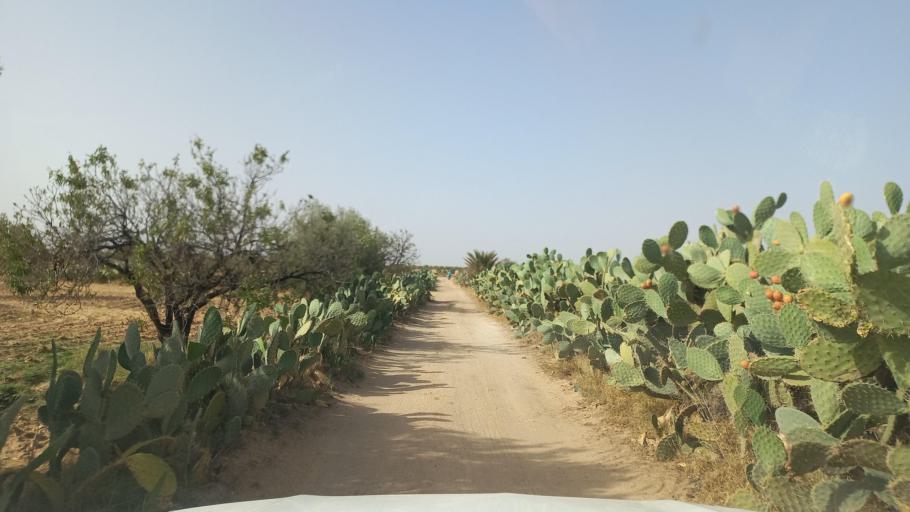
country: TN
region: Al Qasrayn
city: Kasserine
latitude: 35.2971
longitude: 8.9624
